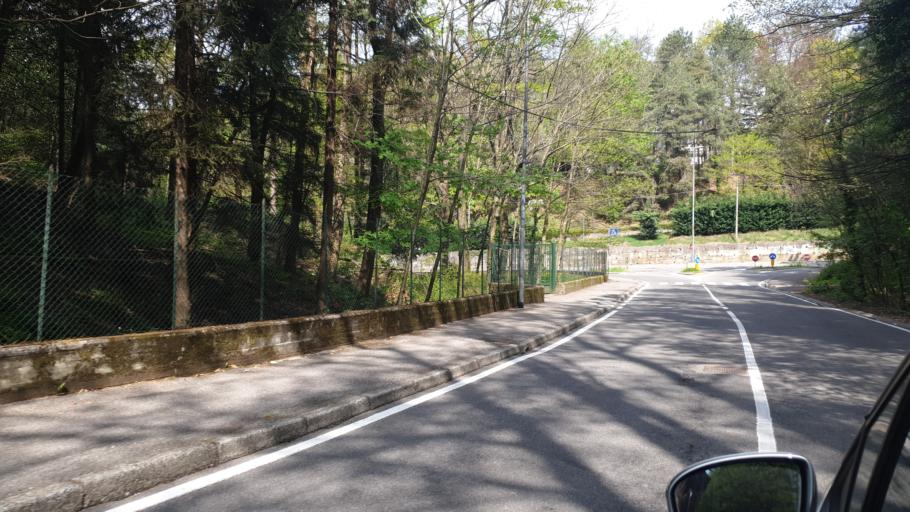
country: IT
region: Lombardy
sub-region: Provincia di Varese
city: Tradate
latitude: 45.7178
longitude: 8.9129
